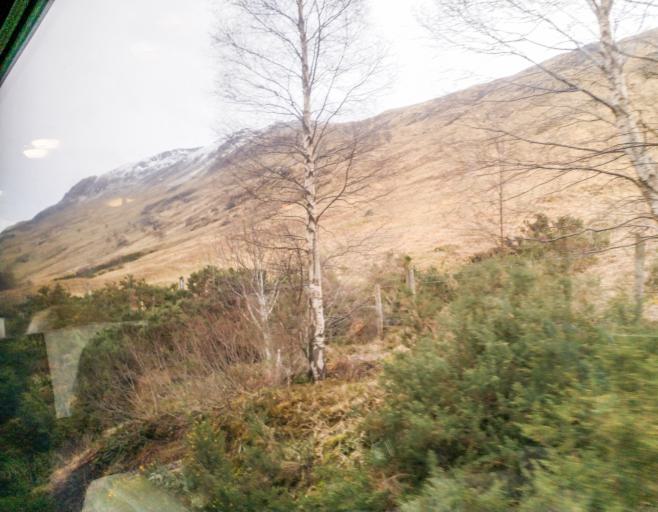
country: GB
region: Scotland
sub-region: Highland
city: Spean Bridge
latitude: 56.8149
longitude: -4.7152
